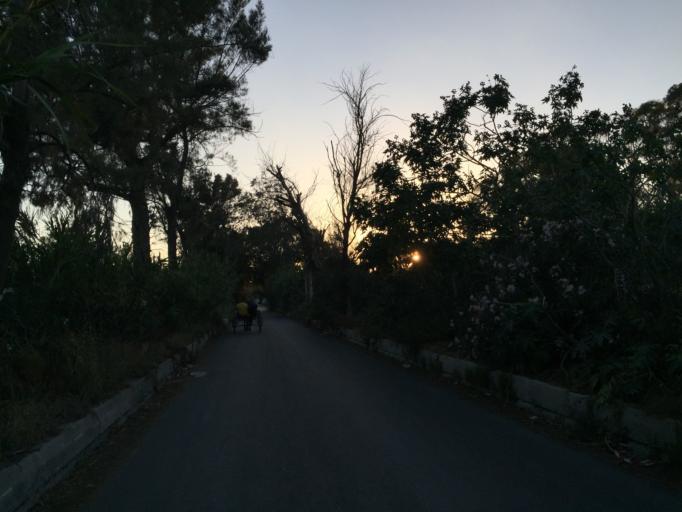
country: MT
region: Il-Marsa
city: Marsa
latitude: 35.8767
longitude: 14.4912
